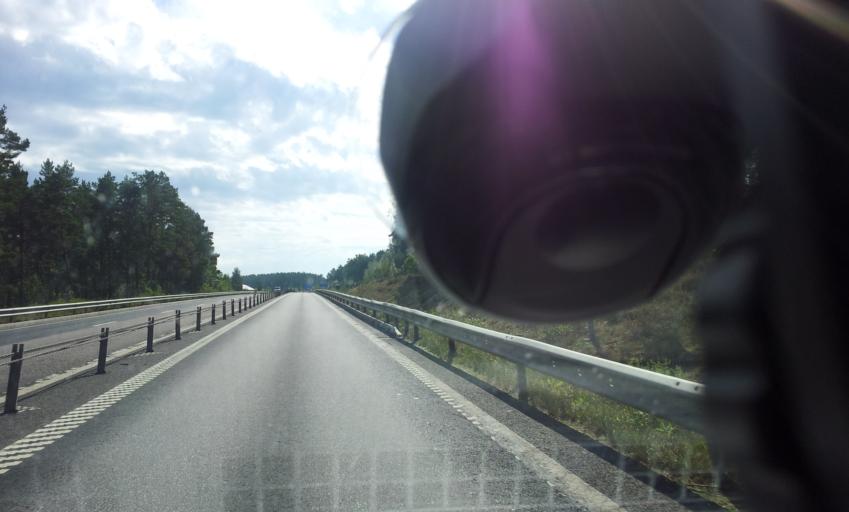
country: SE
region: Kalmar
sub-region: Oskarshamns Kommun
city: Oskarshamn
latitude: 57.3859
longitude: 16.4803
